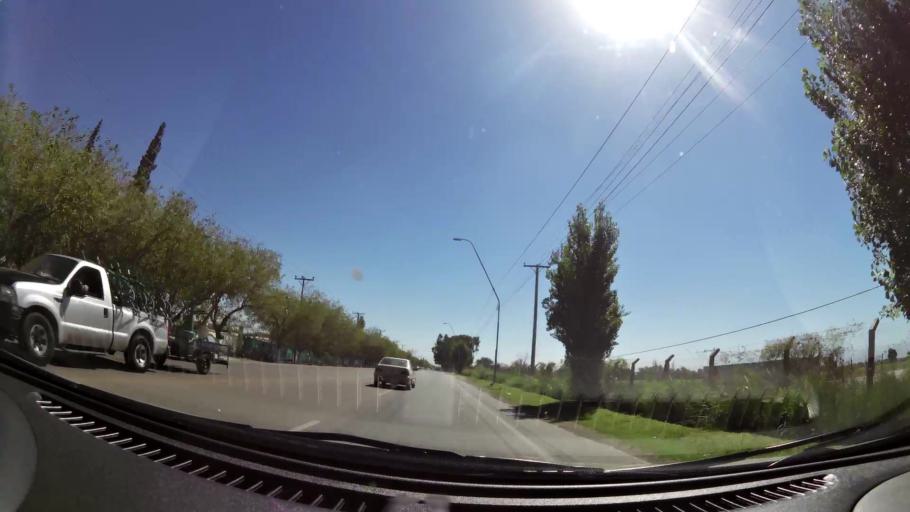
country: AR
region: San Juan
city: Villa Krause
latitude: -31.5986
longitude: -68.5411
